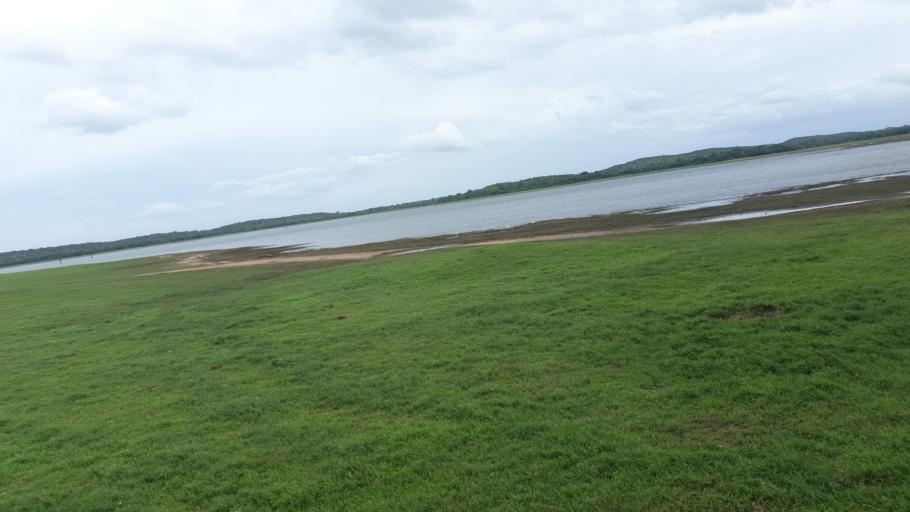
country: LK
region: North Central
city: Polonnaruwa
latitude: 8.1303
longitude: 80.9111
